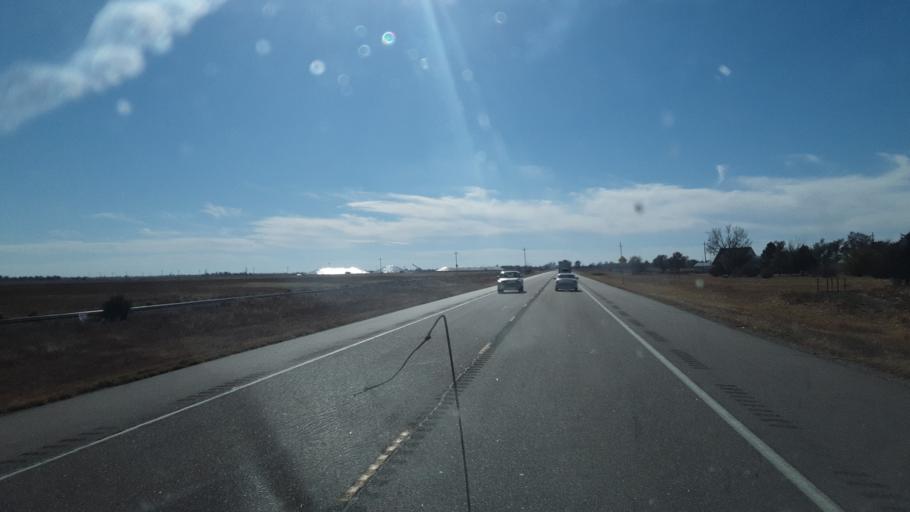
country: US
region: Kansas
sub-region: Pawnee County
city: Larned
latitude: 38.2111
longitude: -99.0564
